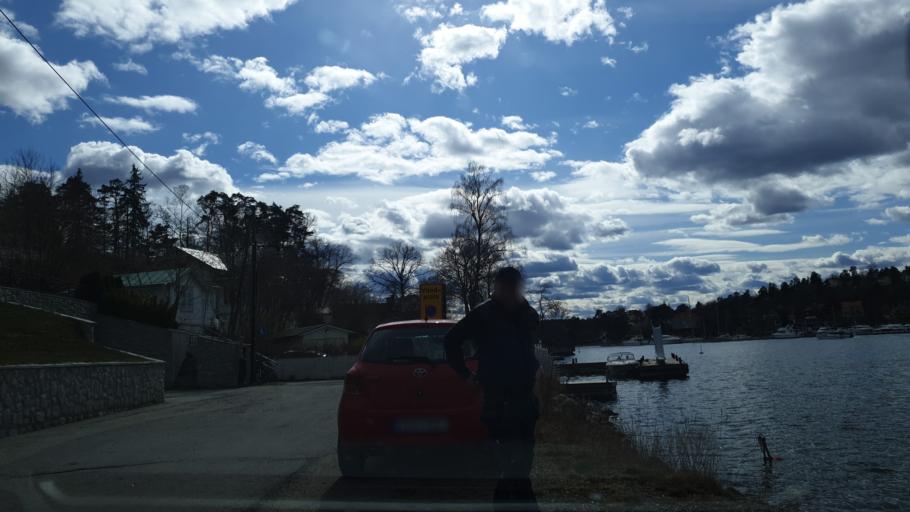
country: SE
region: Stockholm
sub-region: Lidingo
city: Brevik
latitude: 59.3098
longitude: 18.2219
